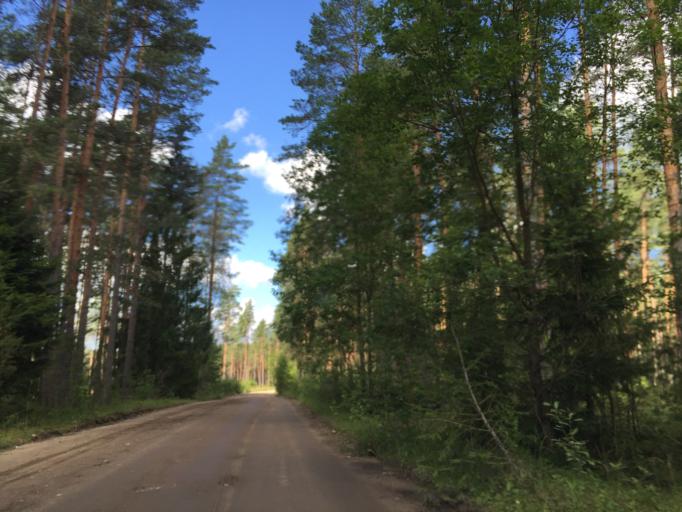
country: LV
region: Garkalne
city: Garkalne
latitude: 56.9713
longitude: 24.4688
